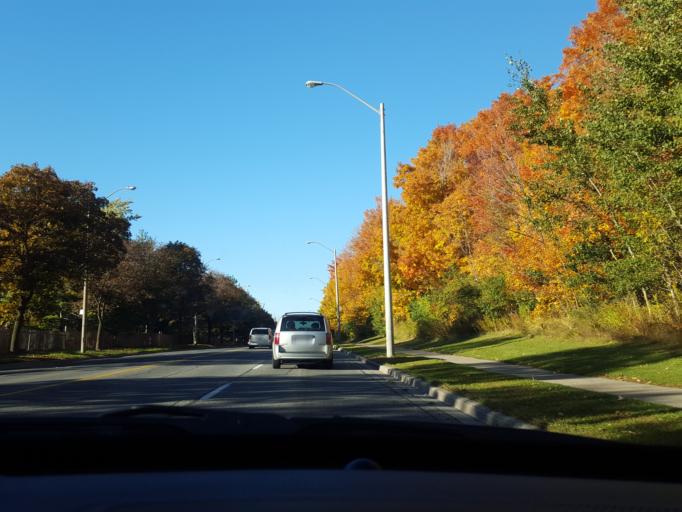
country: CA
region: Ontario
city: Scarborough
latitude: 43.8075
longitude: -79.2781
